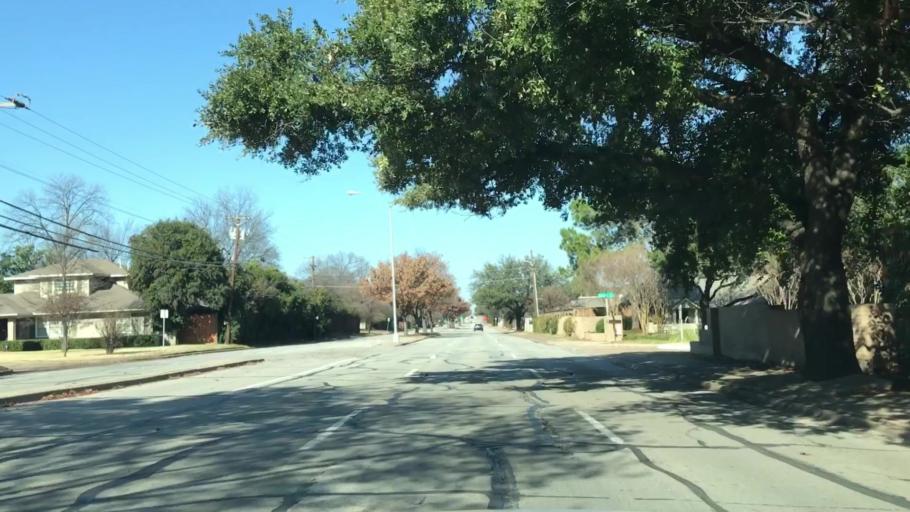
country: US
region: Texas
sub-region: Dallas County
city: University Park
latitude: 32.8741
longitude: -96.7868
